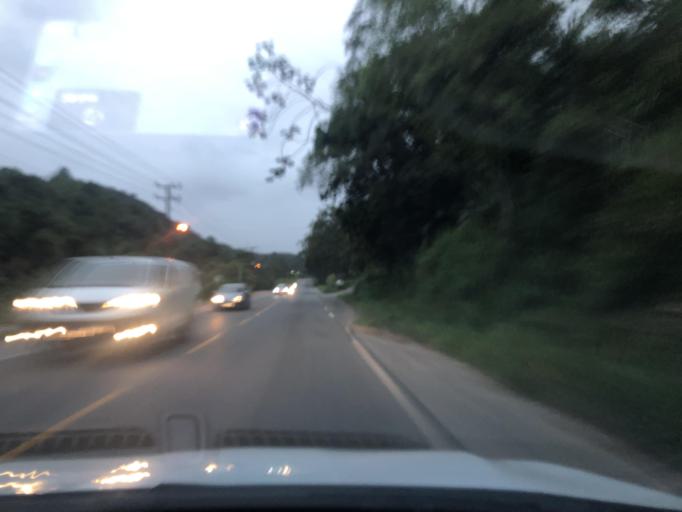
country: BR
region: Santa Catarina
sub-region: Pomerode
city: Pomerode
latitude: -26.7038
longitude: -49.0529
